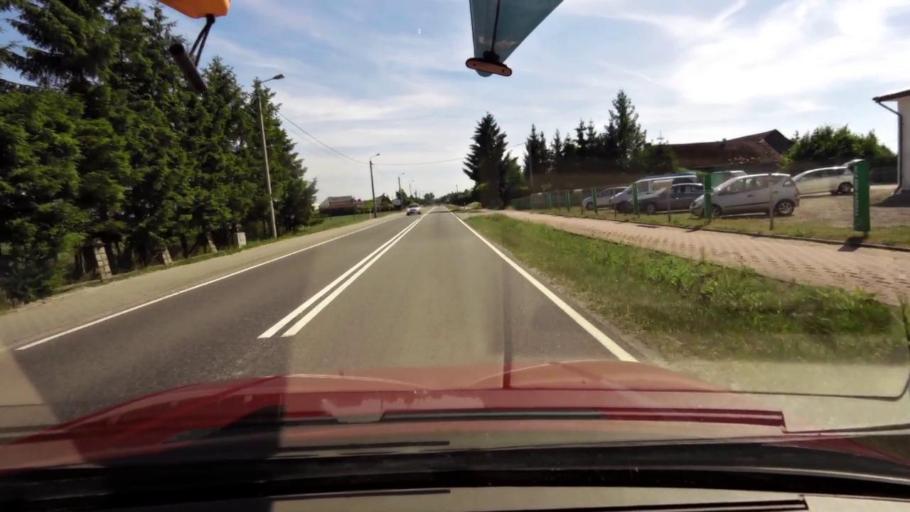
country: PL
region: Pomeranian Voivodeship
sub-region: Powiat slupski
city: Kobylnica
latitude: 54.4197
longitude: 17.0074
